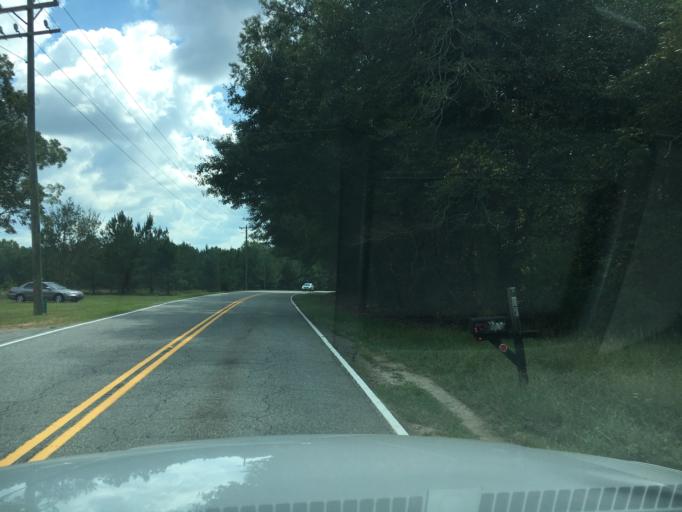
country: US
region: South Carolina
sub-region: Greenwood County
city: Greenwood
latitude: 34.1171
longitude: -82.1266
